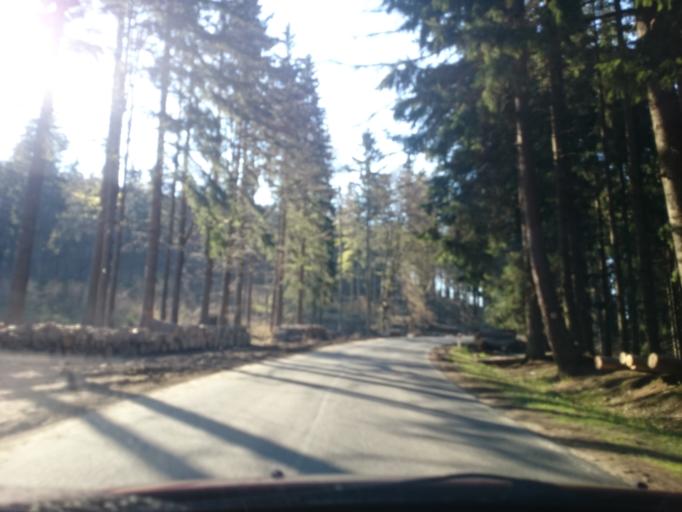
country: PL
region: Lower Silesian Voivodeship
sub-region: Powiat klodzki
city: Duszniki-Zdroj
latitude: 50.3249
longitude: 16.4123
